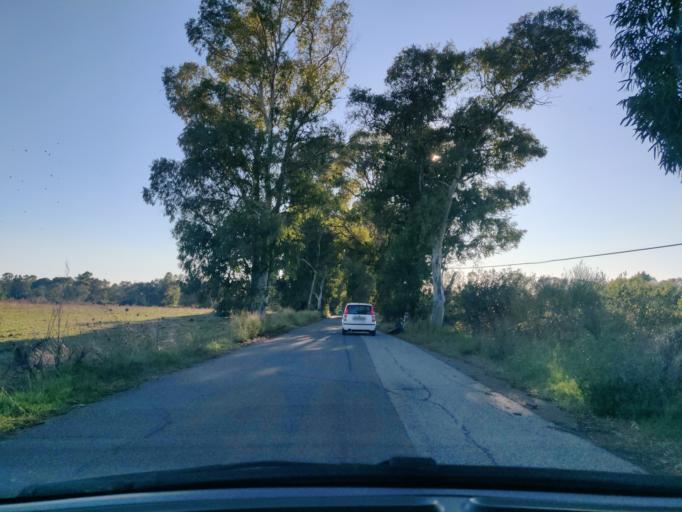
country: IT
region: Latium
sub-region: Citta metropolitana di Roma Capitale
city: Aurelia
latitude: 42.1515
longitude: 11.7504
